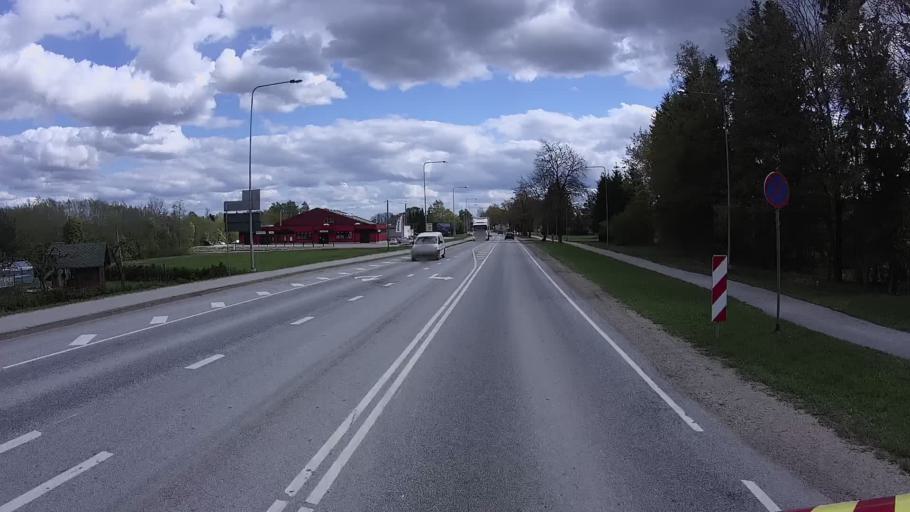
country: EE
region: Jogevamaa
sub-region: Jogeva linn
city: Jogeva
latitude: 58.7421
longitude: 26.3674
